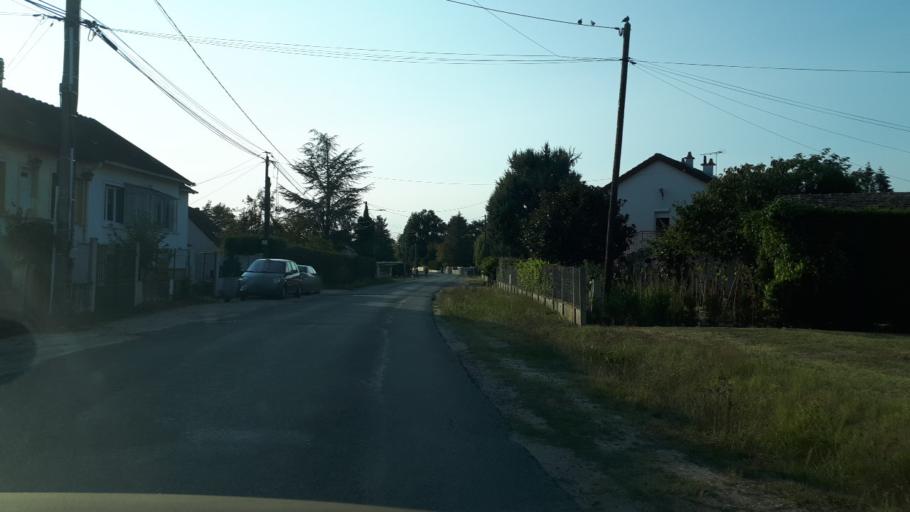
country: FR
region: Centre
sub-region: Departement du Loir-et-Cher
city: Romorantin-Lanthenay
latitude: 47.3435
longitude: 1.7710
